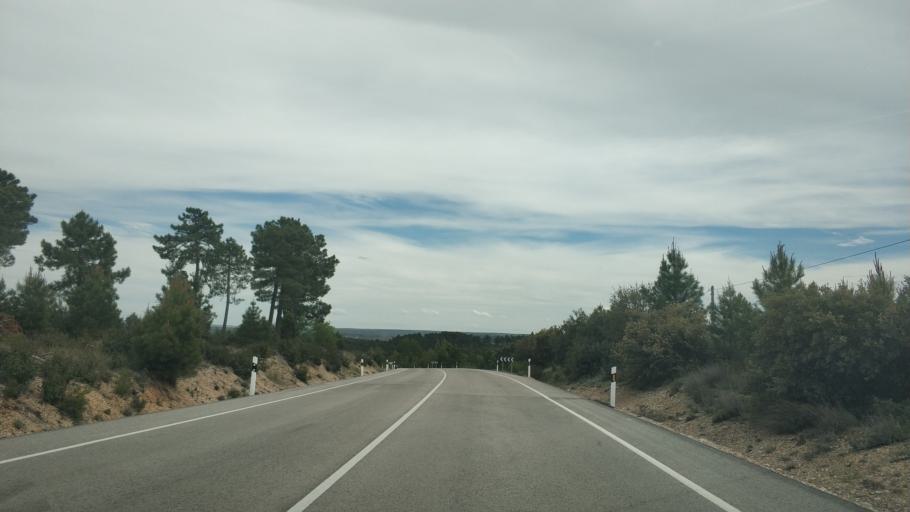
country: ES
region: Castille and Leon
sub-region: Provincia de Soria
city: Quintanas de Gormaz
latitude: 41.5265
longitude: -2.9432
